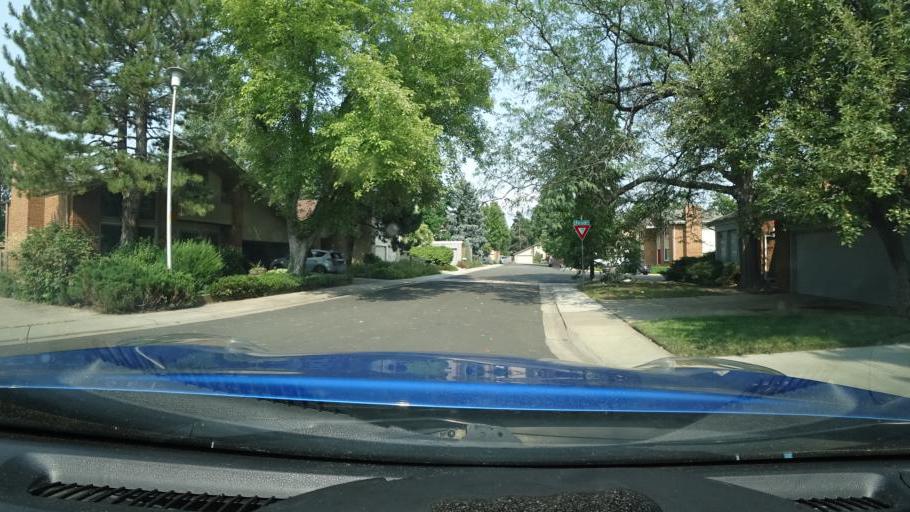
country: US
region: Colorado
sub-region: Adams County
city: Aurora
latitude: 39.6658
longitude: -104.8522
